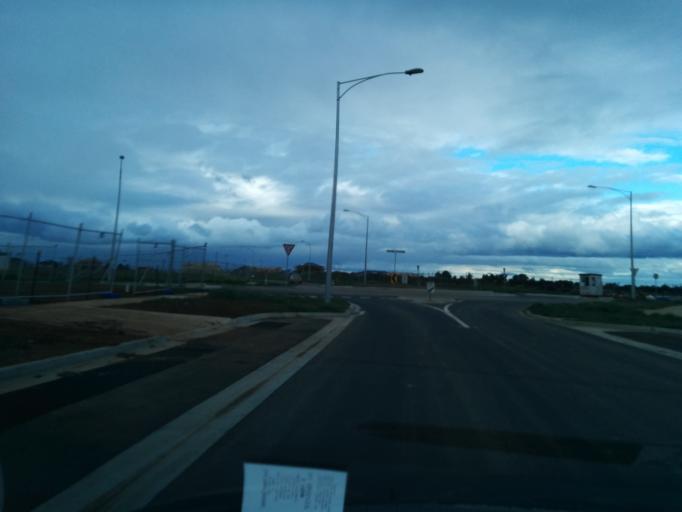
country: AU
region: Victoria
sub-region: Wyndham
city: Point Cook
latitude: -37.9112
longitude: 144.7451
